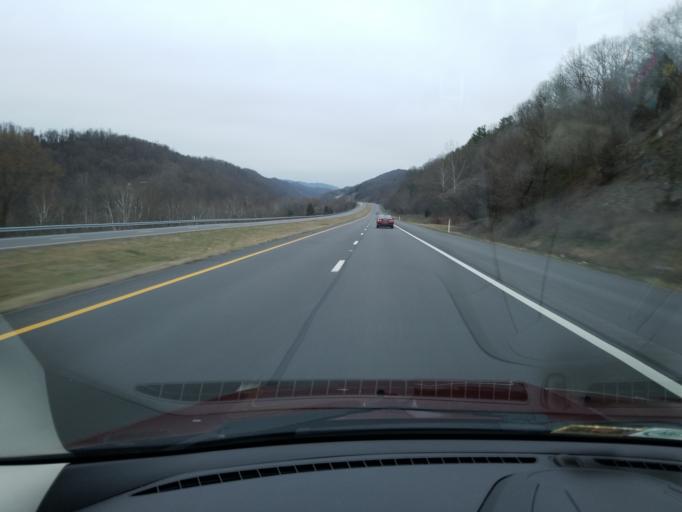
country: US
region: Virginia
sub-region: Giles County
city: Narrows
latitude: 37.3574
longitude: -80.8939
